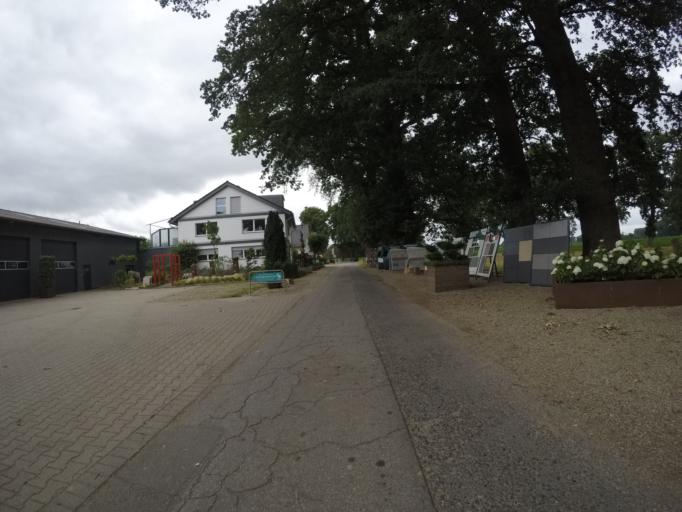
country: DE
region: North Rhine-Westphalia
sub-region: Regierungsbezirk Dusseldorf
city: Hamminkeln
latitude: 51.7666
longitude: 6.6031
